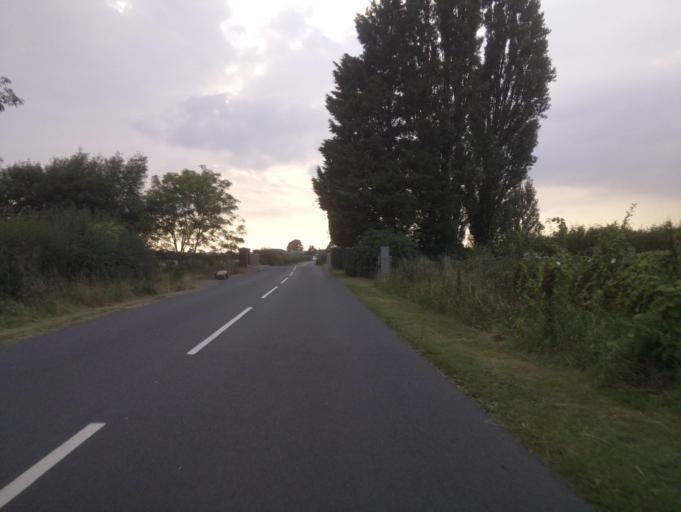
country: GB
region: England
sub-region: Lincolnshire
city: Skellingthorpe
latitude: 53.1339
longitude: -0.6418
